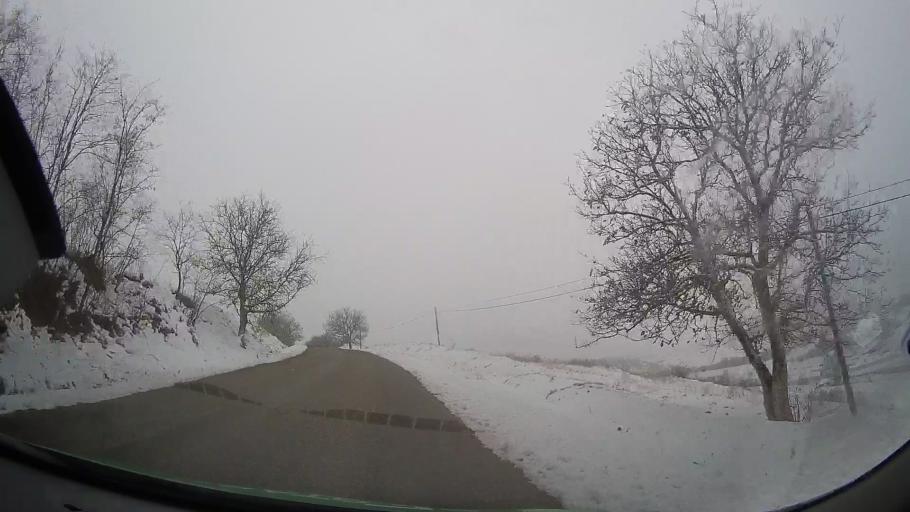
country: RO
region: Bacau
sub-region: Comuna Vultureni
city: Vultureni
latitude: 46.3773
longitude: 27.2761
